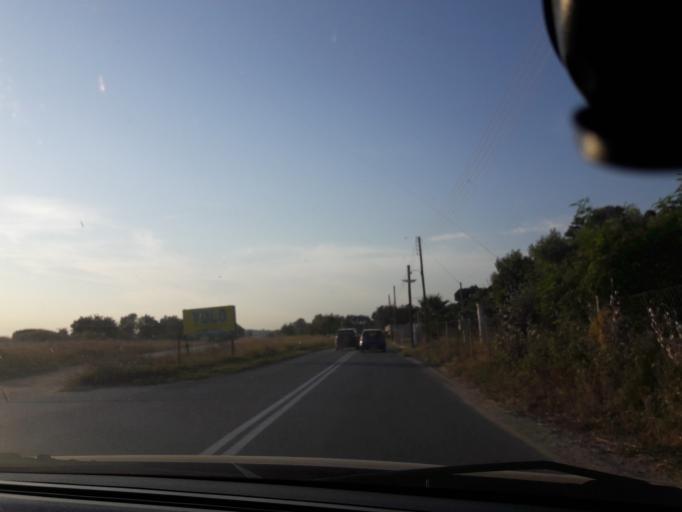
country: GR
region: Central Macedonia
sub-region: Nomos Chalkidikis
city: Nea Kallikrateia
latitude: 40.3322
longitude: 23.0242
